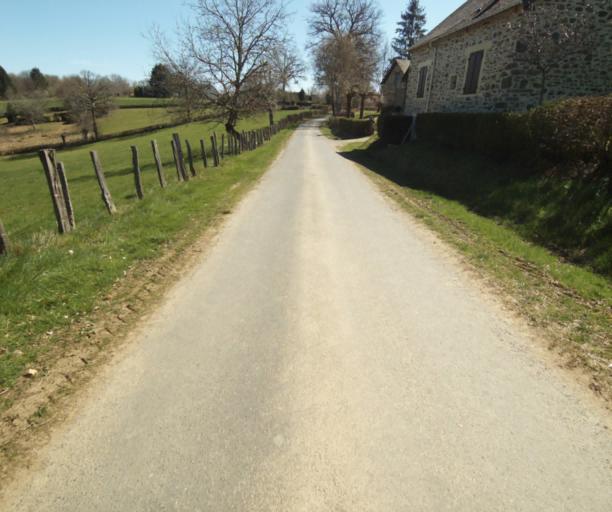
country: FR
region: Limousin
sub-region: Departement de la Correze
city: Chamboulive
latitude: 45.4399
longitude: 1.6858
